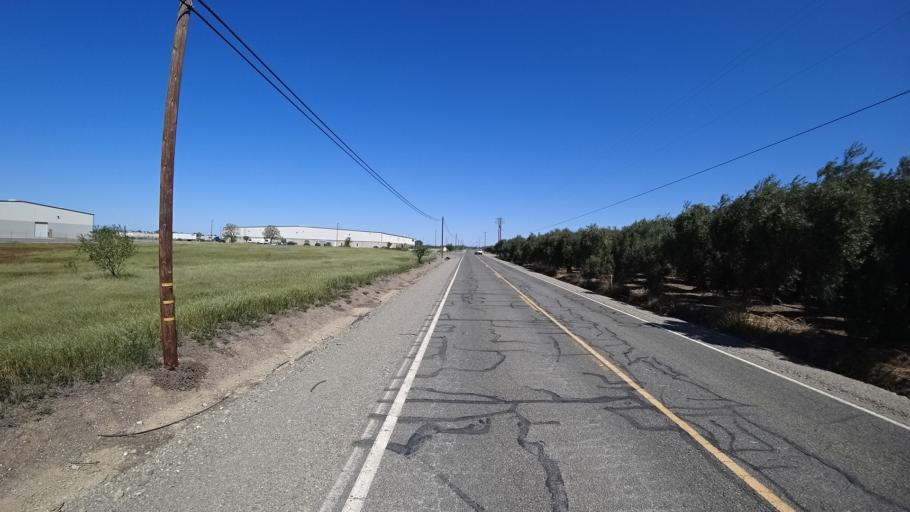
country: US
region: California
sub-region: Glenn County
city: Orland
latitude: 39.7168
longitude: -122.1411
